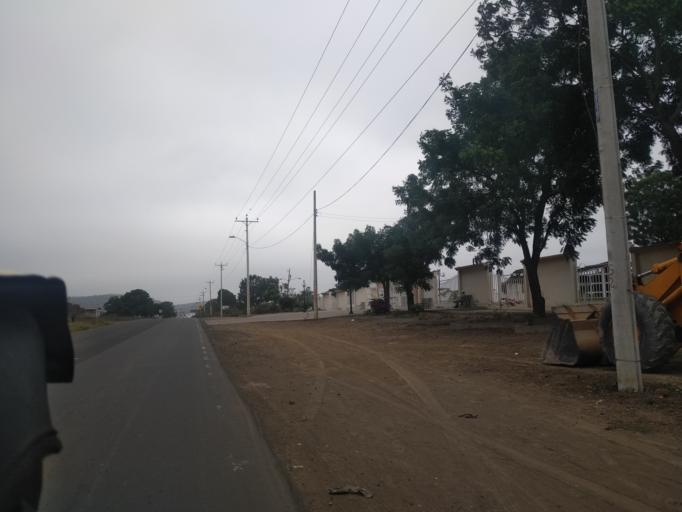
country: EC
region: Manabi
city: Montecristi
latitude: -1.0812
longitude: -80.6755
